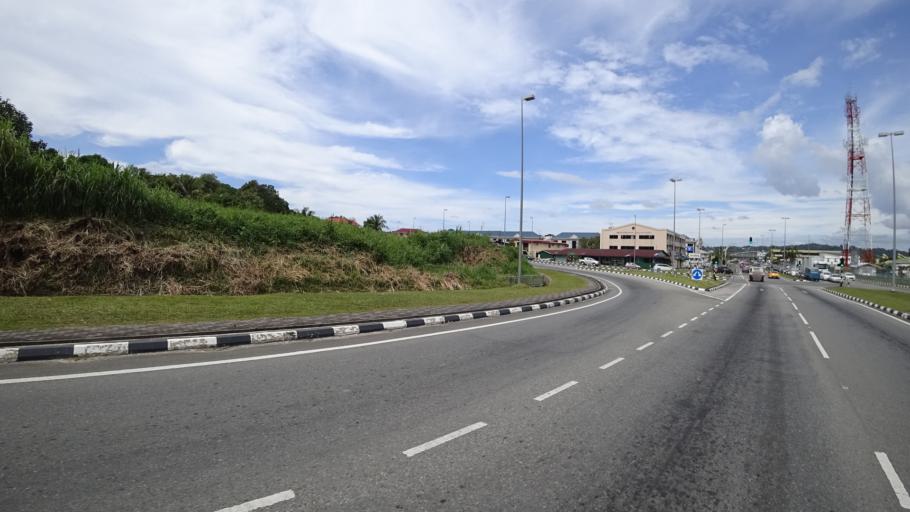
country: BN
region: Brunei and Muara
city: Bandar Seri Begawan
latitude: 4.8853
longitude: 114.8382
